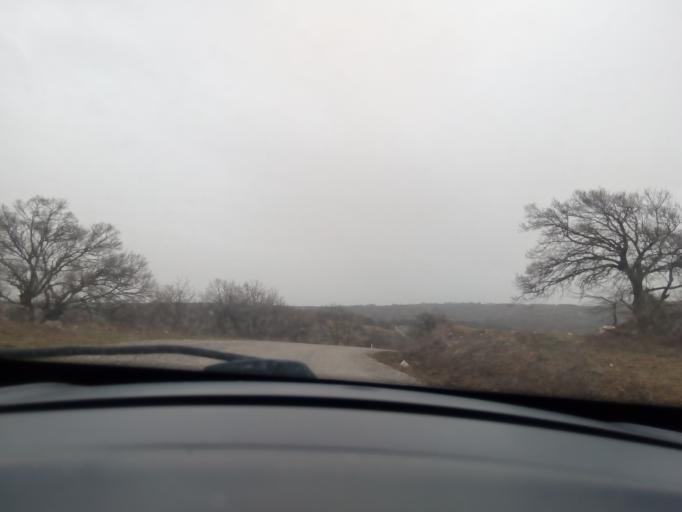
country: TR
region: Balikesir
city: Susurluk
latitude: 39.9210
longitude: 28.0783
